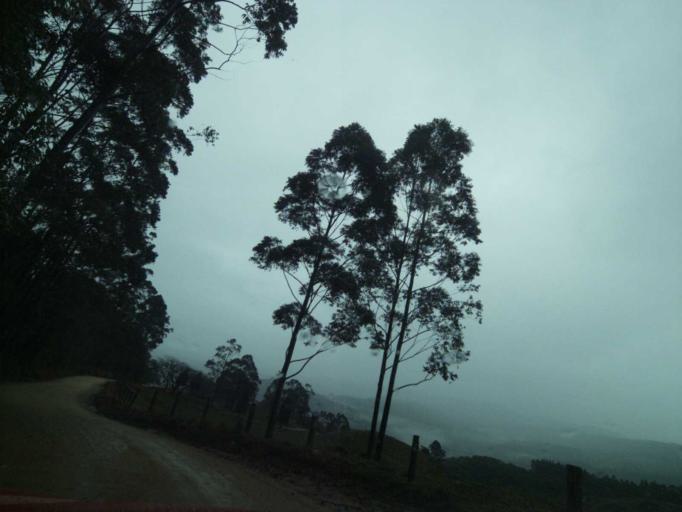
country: BR
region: Santa Catarina
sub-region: Anitapolis
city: Anitapolis
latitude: -27.9194
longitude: -49.1775
